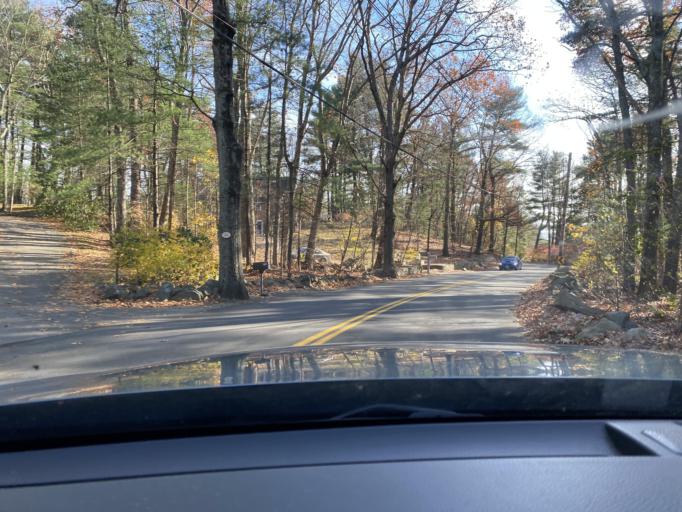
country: US
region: Massachusetts
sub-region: Norfolk County
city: Westwood
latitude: 42.1864
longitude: -71.2383
